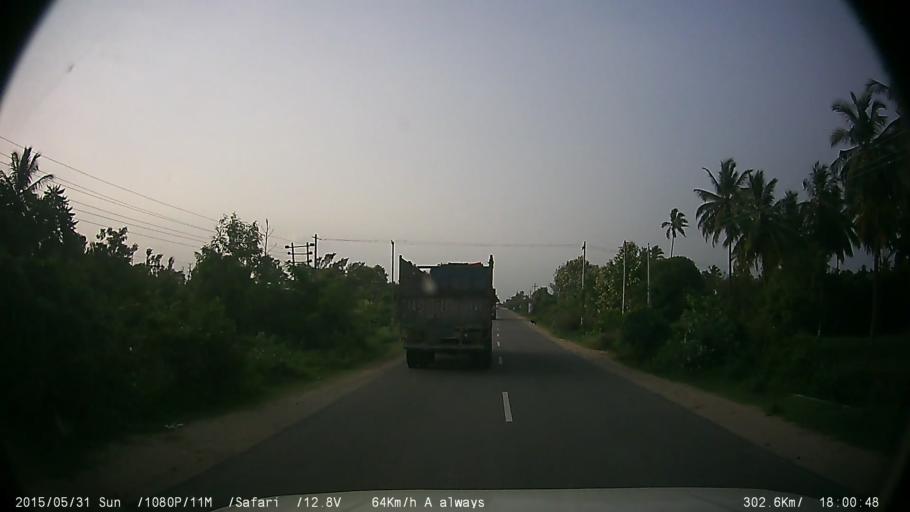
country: IN
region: Karnataka
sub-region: Mysore
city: Nanjangud
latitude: 12.0241
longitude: 76.6733
